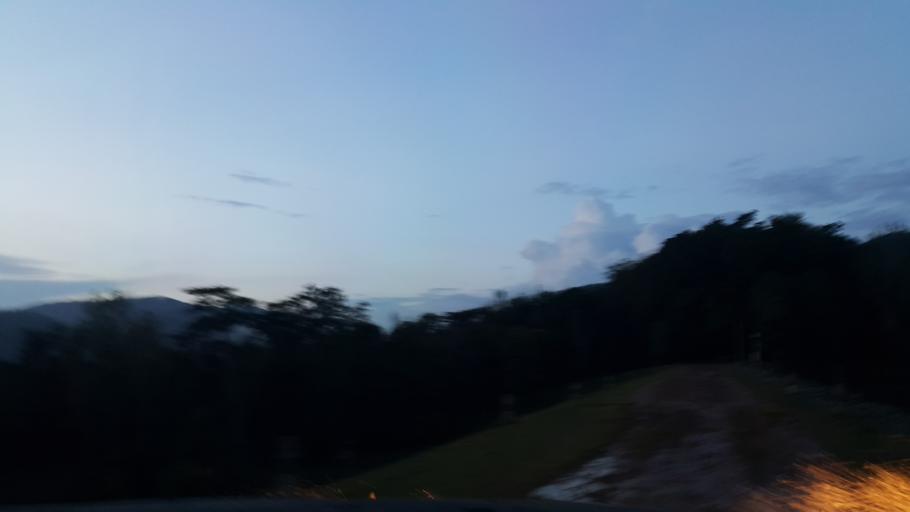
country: TH
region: Chiang Mai
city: Mae On
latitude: 18.7326
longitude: 99.3095
